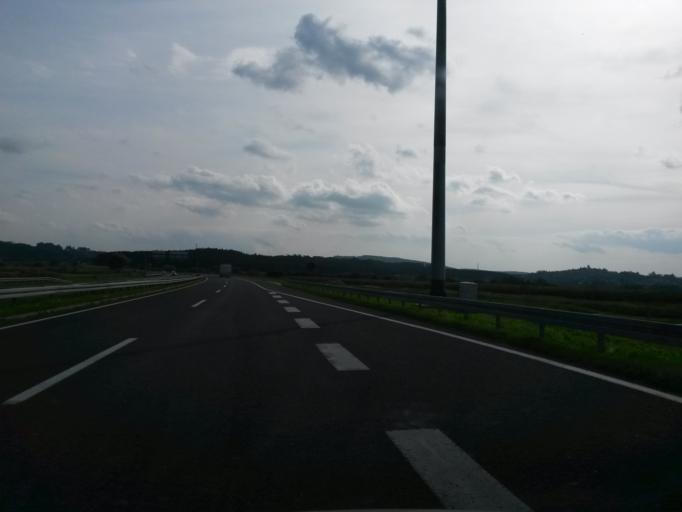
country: HR
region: Medimurska
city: Kursanec
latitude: 46.2579
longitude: 16.3990
